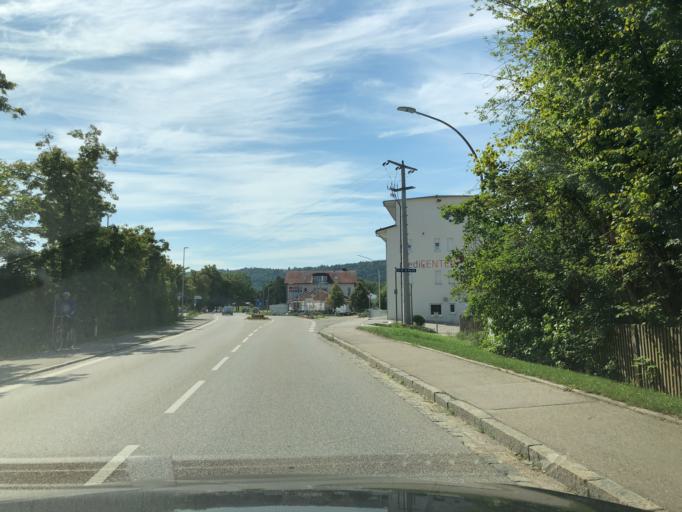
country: DE
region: Bavaria
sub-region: Upper Palatinate
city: Berching
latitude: 49.0312
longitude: 11.4765
